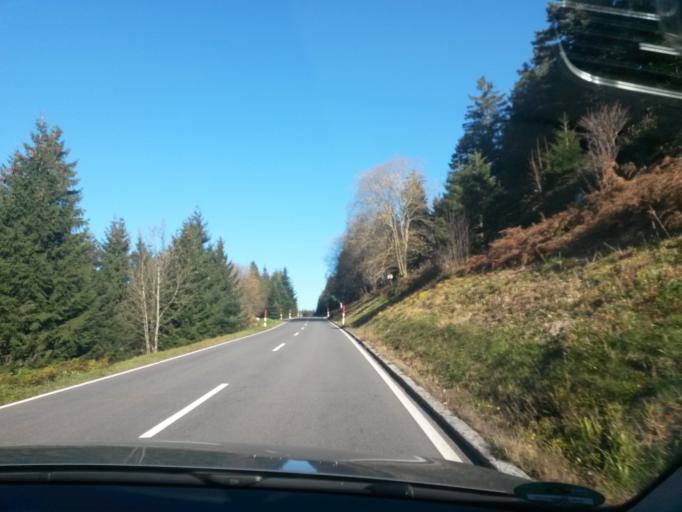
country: DE
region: Baden-Wuerttemberg
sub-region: Karlsruhe Region
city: Bad Rippoldsau-Schapbach
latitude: 48.4572
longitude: 8.2953
